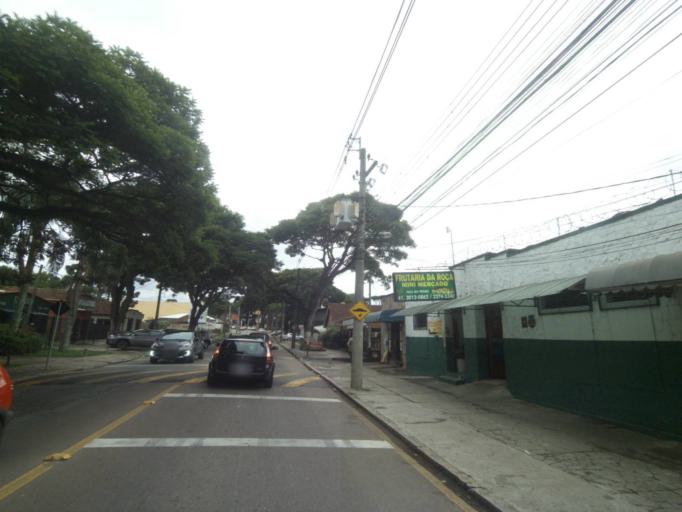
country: BR
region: Parana
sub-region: Curitiba
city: Curitiba
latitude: -25.4505
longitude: -49.3147
